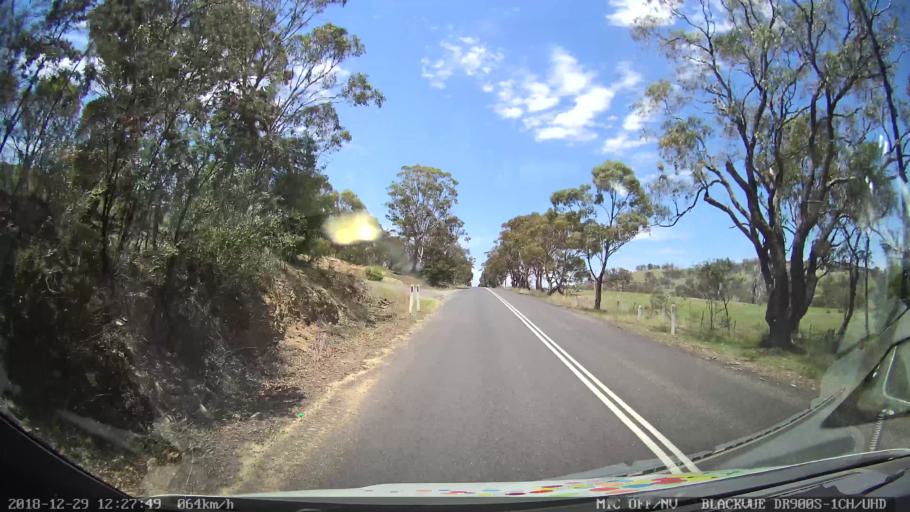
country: AU
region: Australian Capital Territory
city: Macarthur
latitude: -35.4804
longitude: 149.2243
